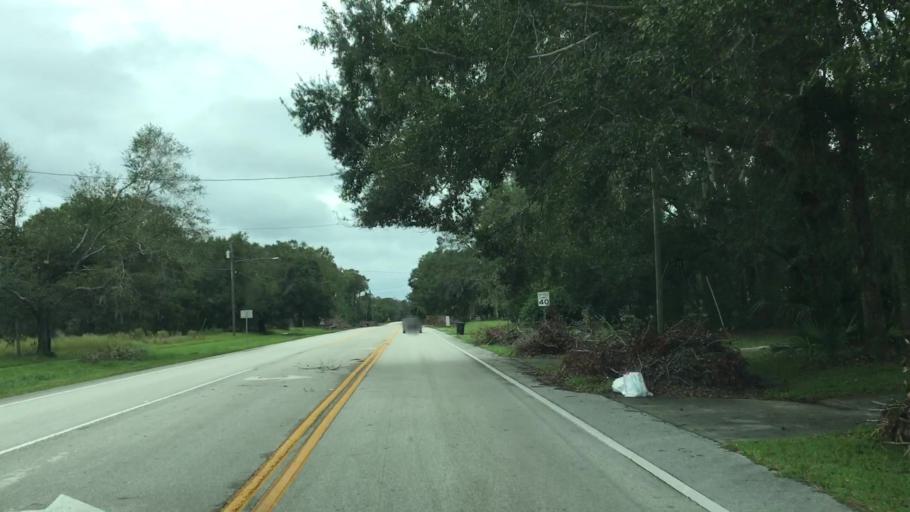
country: US
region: Florida
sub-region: Volusia County
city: Lake Helen
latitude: 28.9852
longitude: -81.2236
